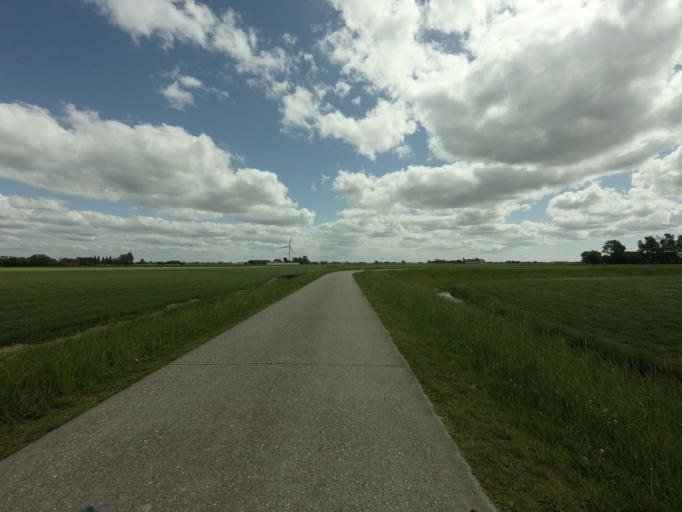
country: NL
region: Friesland
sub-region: Gemeente Littenseradiel
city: Wommels
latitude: 53.1221
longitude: 5.5543
